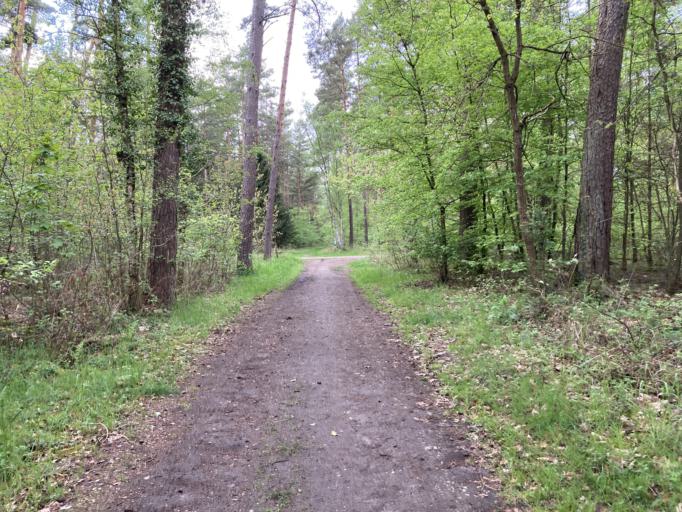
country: DE
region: Lower Saxony
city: Lueneburg
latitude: 53.2303
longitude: 10.4277
